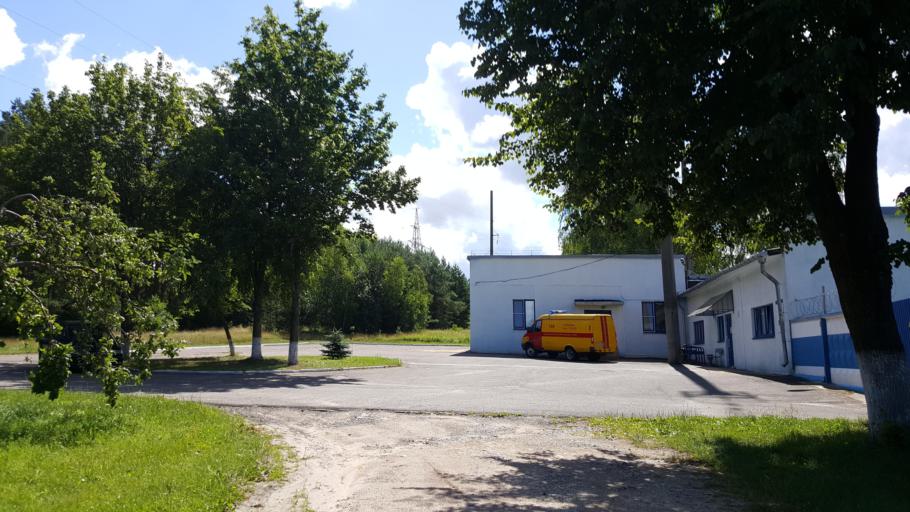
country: BY
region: Brest
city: Kamyanyets
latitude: 52.3907
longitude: 23.8365
